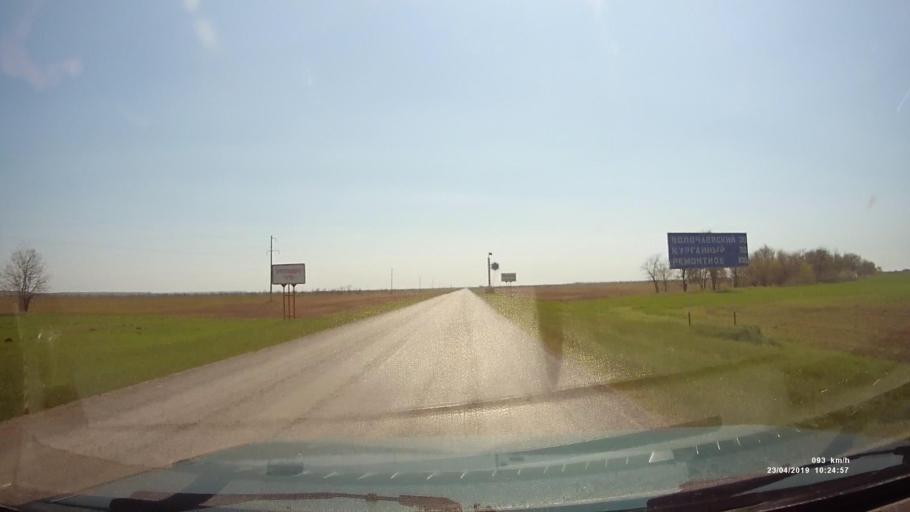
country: RU
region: Rostov
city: Sovetskoye
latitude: 46.6348
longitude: 42.4496
